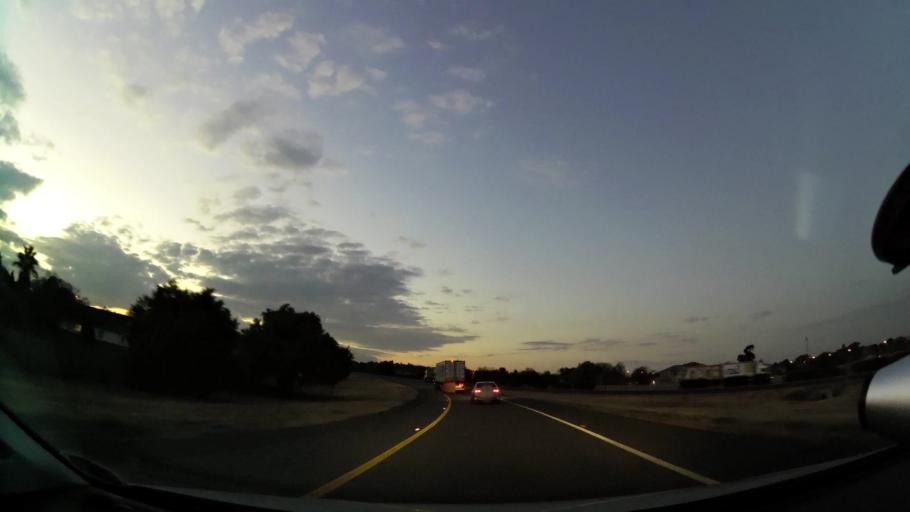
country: ZA
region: Orange Free State
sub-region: Mangaung Metropolitan Municipality
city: Bloemfontein
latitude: -29.1642
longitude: 26.1800
